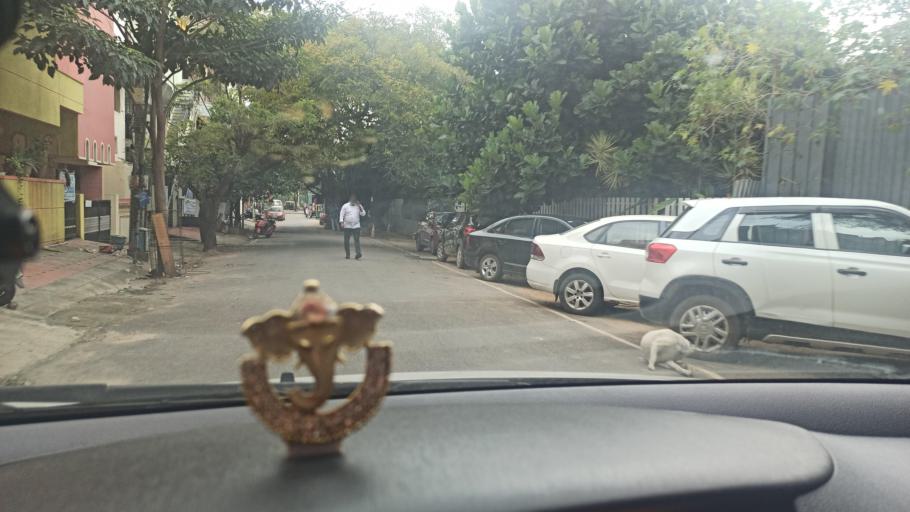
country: IN
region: Karnataka
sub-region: Bangalore Urban
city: Bangalore
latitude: 12.9182
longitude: 77.6287
